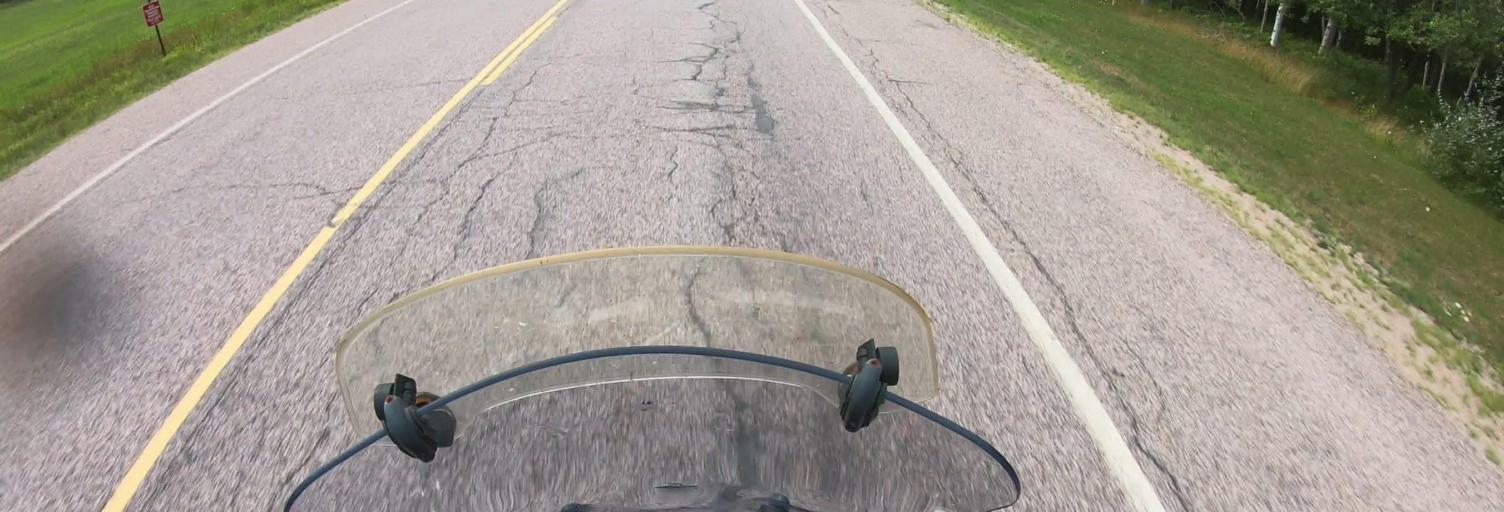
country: US
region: Michigan
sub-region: Marquette County
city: Harvey
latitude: 46.4632
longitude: -87.3262
